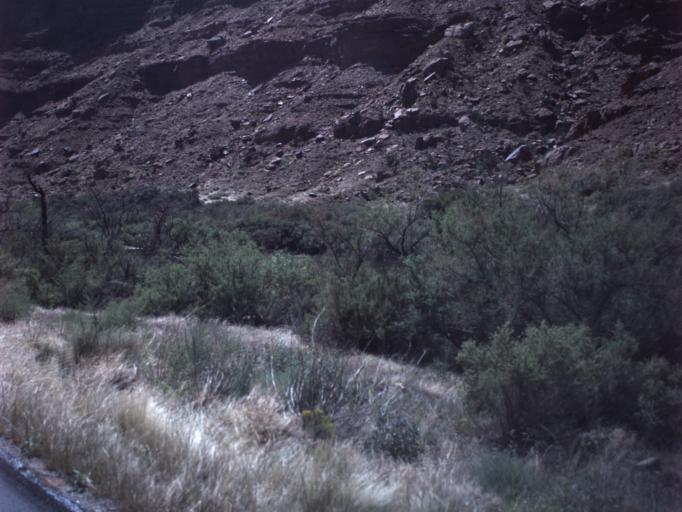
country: US
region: Utah
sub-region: Grand County
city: Moab
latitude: 38.6508
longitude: -109.5057
